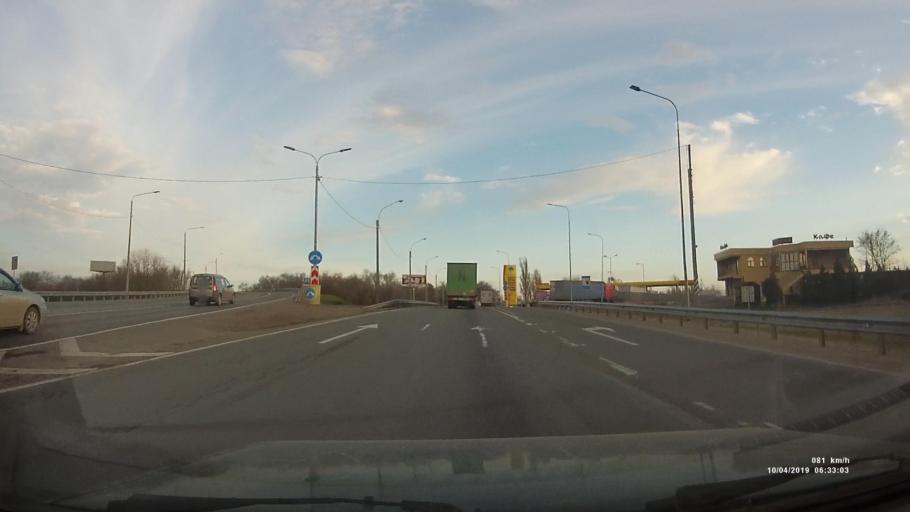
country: RU
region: Rostov
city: Aksay
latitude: 47.2814
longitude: 39.8511
